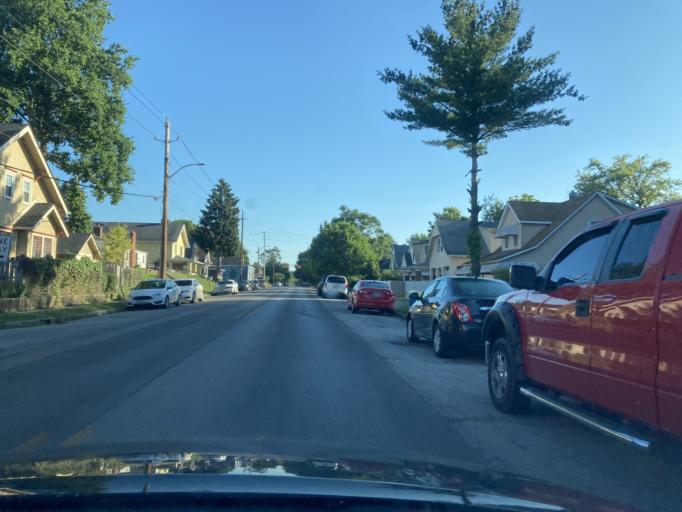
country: US
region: Indiana
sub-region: Marion County
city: Broad Ripple
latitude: 39.8268
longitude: -86.1640
